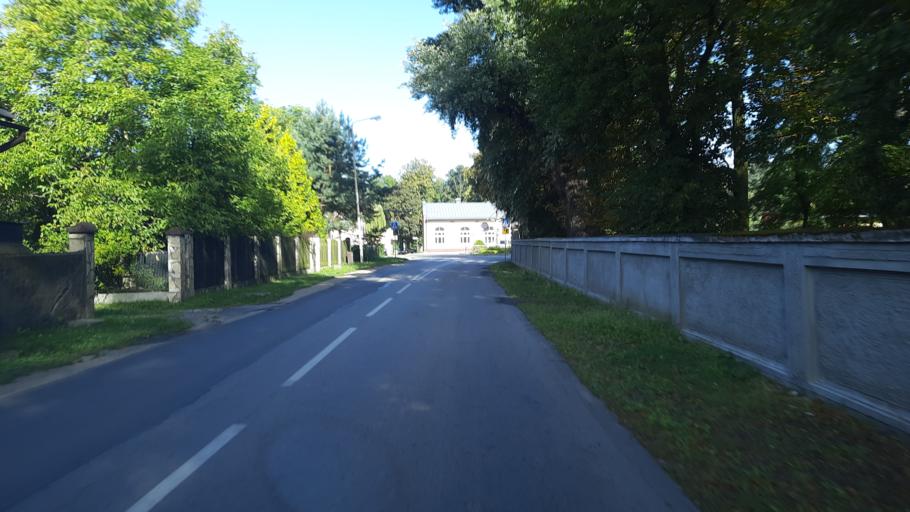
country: PL
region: Lower Silesian Voivodeship
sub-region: Powiat wroclawski
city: Dlugoleka
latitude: 51.1937
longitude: 17.1835
